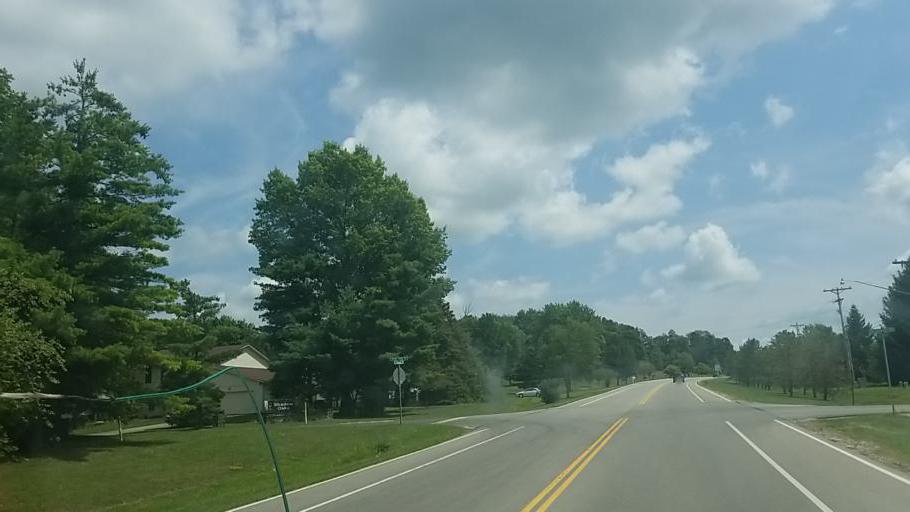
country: US
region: Ohio
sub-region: Fairfield County
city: Pickerington
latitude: 39.8835
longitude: -82.7429
